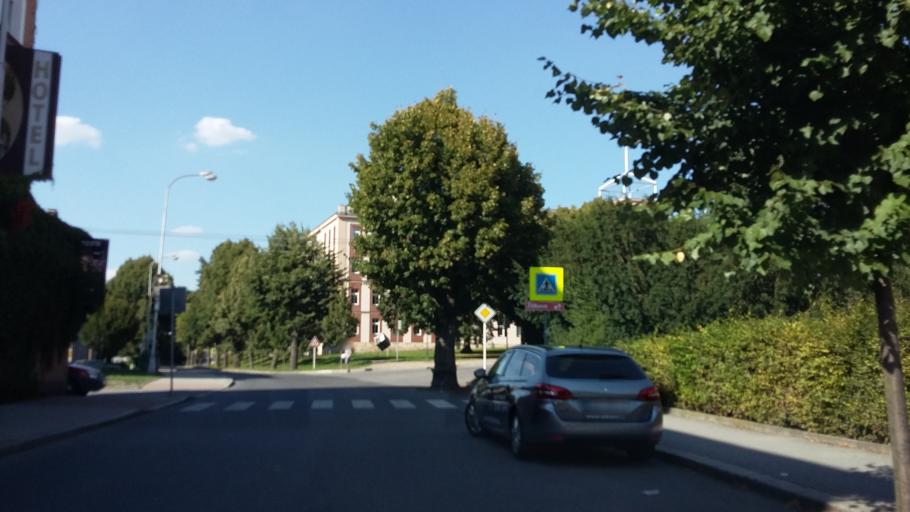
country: CZ
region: Liberecky
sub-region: Okres Semily
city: Turnov
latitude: 50.5927
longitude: 15.1623
